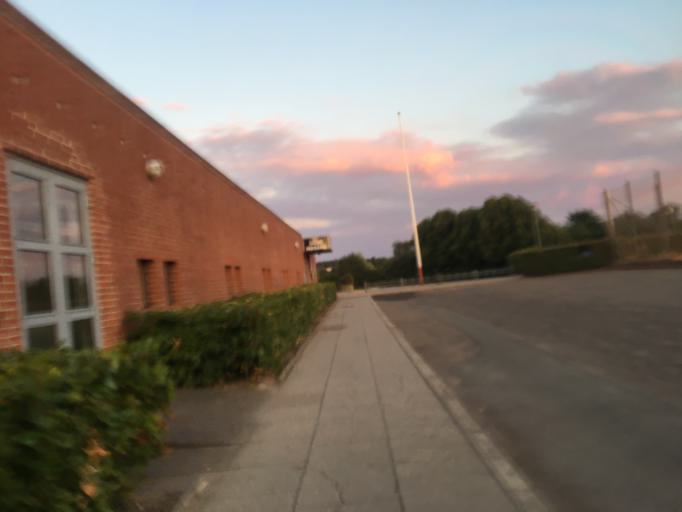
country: DK
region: Central Jutland
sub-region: Syddjurs Kommune
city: Hornslet
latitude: 56.3186
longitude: 10.3243
